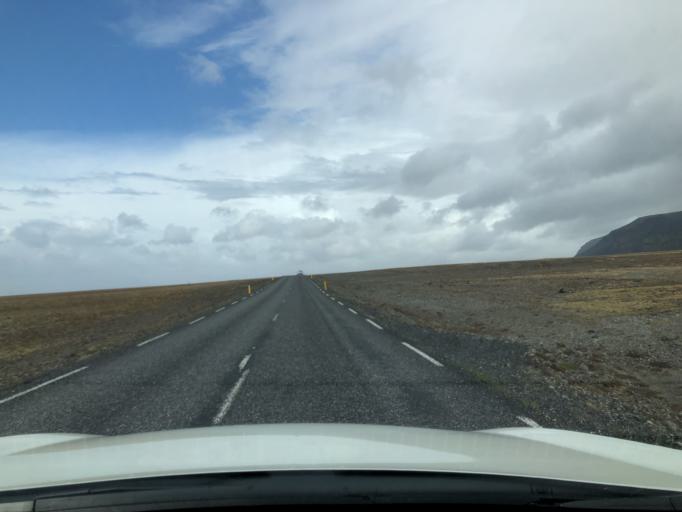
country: IS
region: East
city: Hoefn
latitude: 63.9109
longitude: -16.7367
